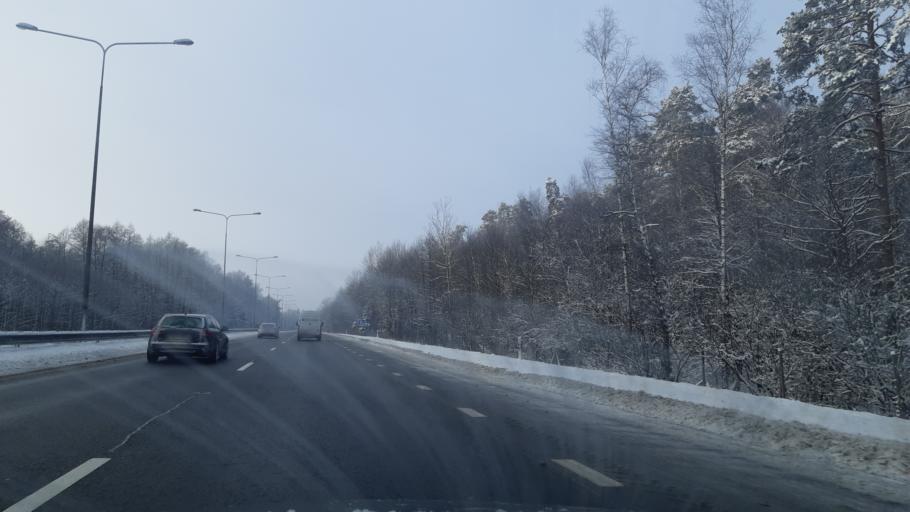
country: LT
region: Kauno apskritis
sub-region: Kauno rajonas
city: Karmelava
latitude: 54.8865
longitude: 24.1799
